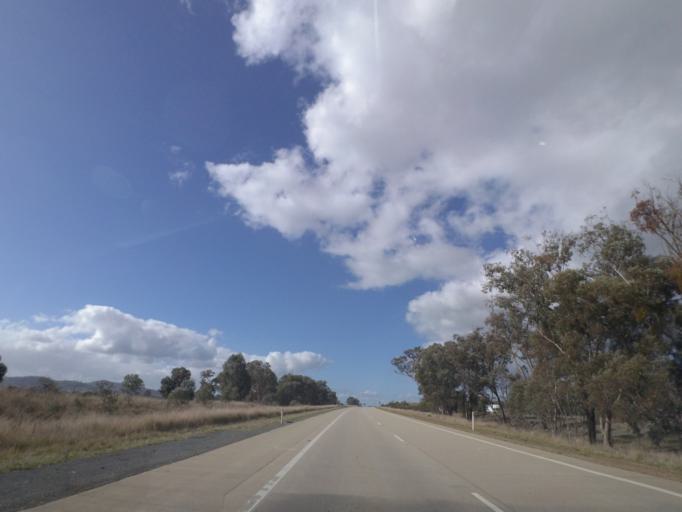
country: AU
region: New South Wales
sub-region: Greater Hume Shire
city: Holbrook
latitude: -35.6867
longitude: 147.3541
